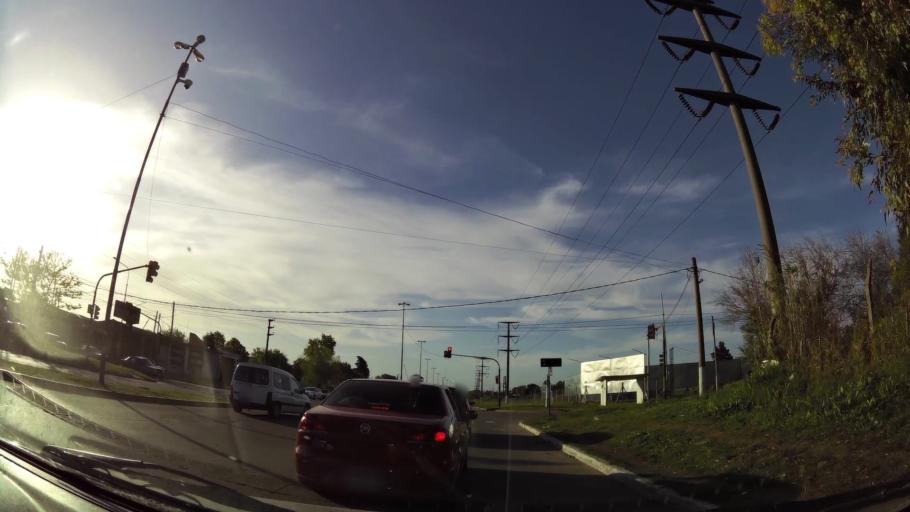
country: AR
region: Buenos Aires
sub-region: Partido de Quilmes
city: Quilmes
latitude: -34.7900
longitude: -58.2175
